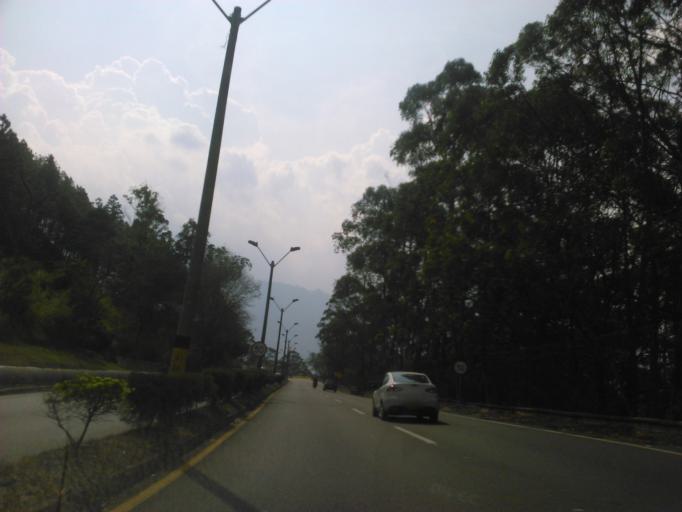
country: CO
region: Antioquia
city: Bello
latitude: 6.3235
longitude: -75.5357
